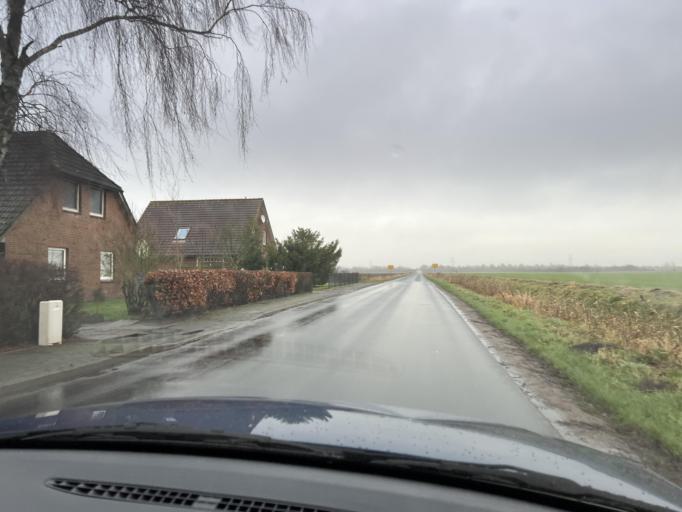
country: DE
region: Schleswig-Holstein
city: Norderwohrden
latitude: 54.2162
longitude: 9.0273
